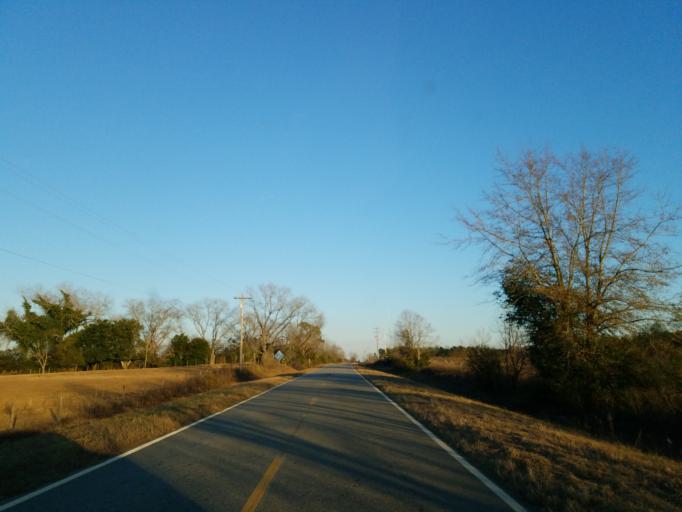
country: US
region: Georgia
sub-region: Worth County
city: Sylvester
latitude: 31.5668
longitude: -83.7049
